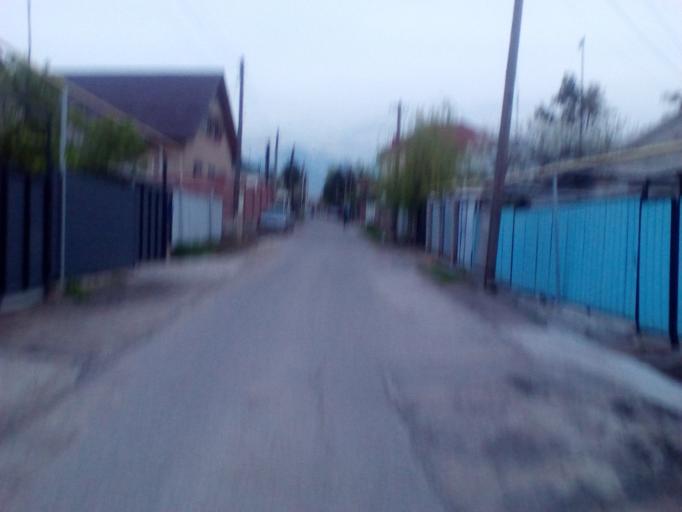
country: KZ
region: Almaty Qalasy
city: Almaty
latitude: 43.2138
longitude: 76.8355
